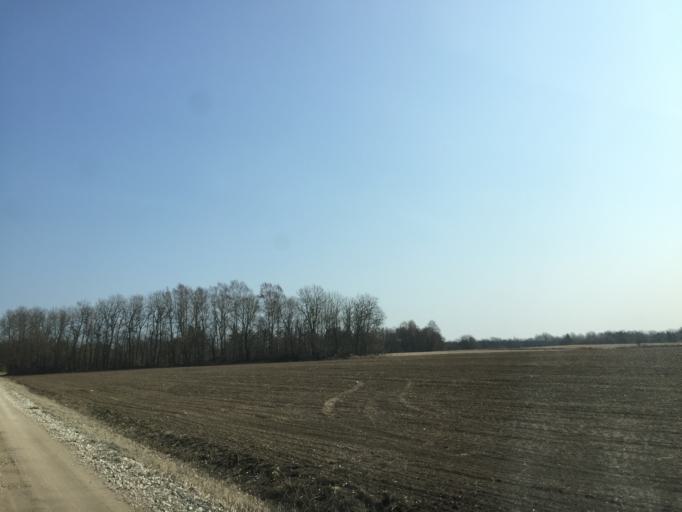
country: EE
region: Saare
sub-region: Kuressaare linn
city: Kuressaare
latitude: 58.3799
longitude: 22.7154
